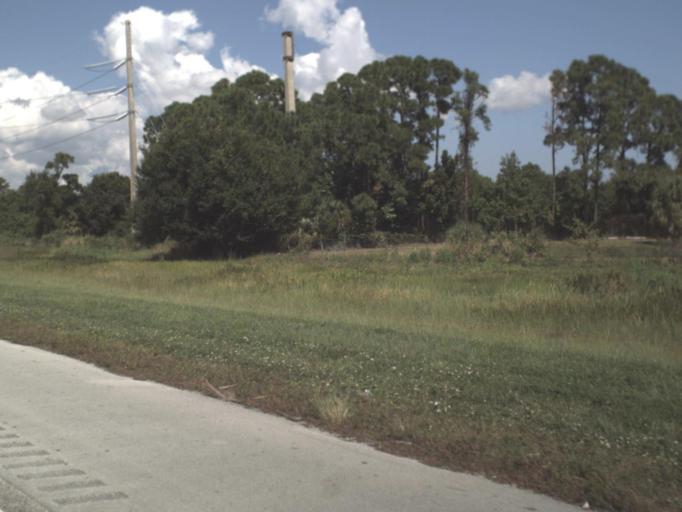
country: US
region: Florida
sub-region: Martin County
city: Palm City
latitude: 27.1643
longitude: -80.3065
